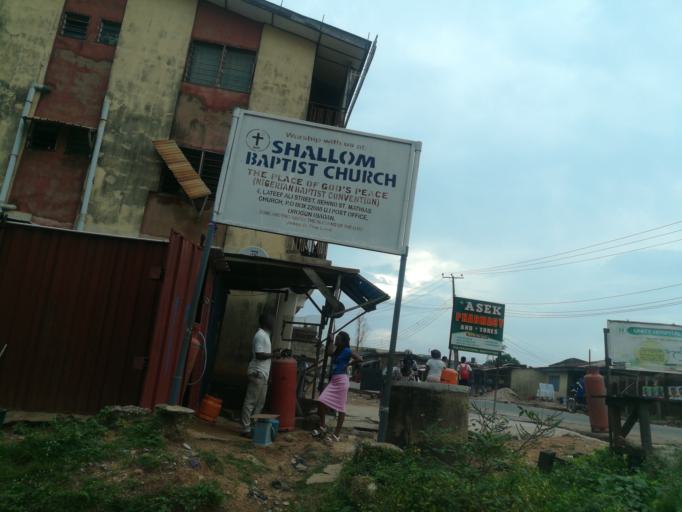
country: NG
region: Oyo
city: Moniya
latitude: 7.4545
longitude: 3.9159
